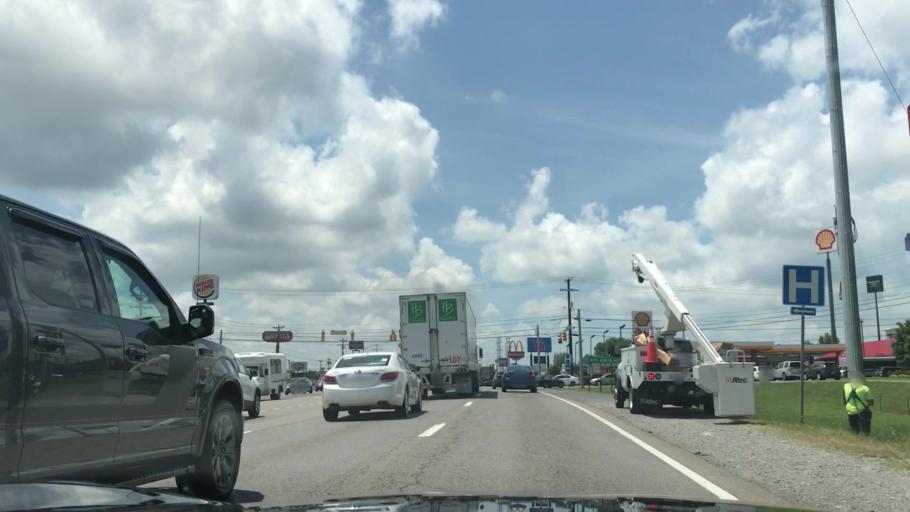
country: US
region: Tennessee
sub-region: Montgomery County
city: Clarksville
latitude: 36.5980
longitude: -87.2849
